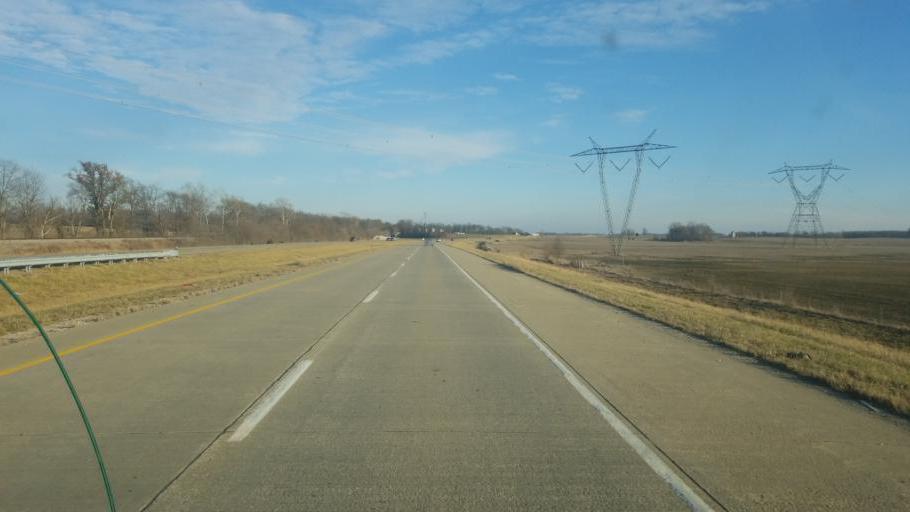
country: US
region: Indiana
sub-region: Knox County
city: Bicknell
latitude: 38.6681
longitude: -87.3343
